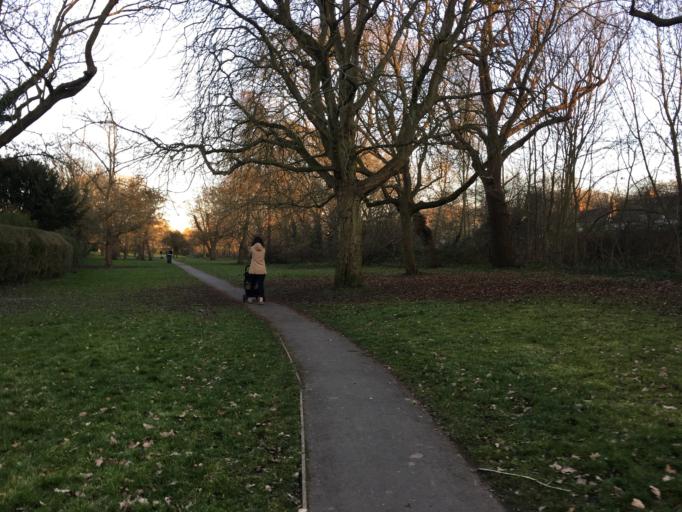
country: GB
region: England
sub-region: Greater London
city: Hendon
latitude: 51.5862
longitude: -0.1897
